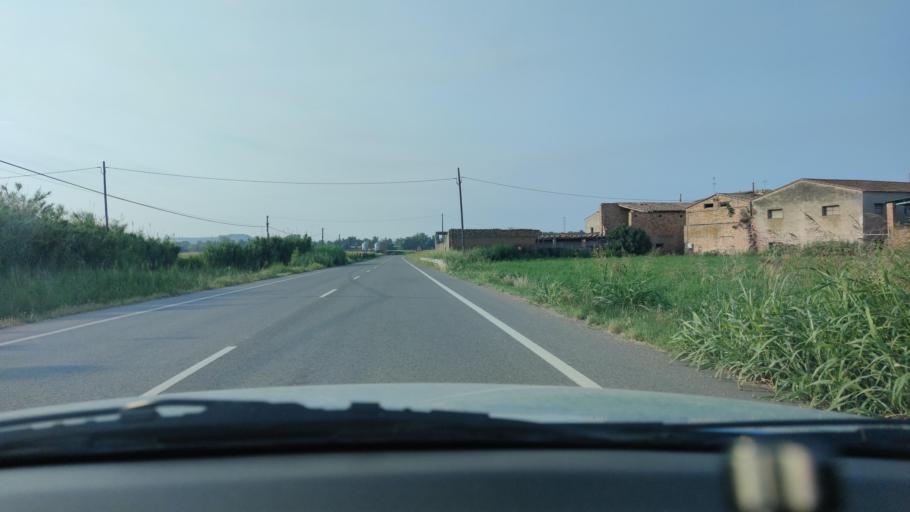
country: ES
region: Catalonia
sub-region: Provincia de Lleida
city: Torres de Segre
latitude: 41.5462
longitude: 0.5114
